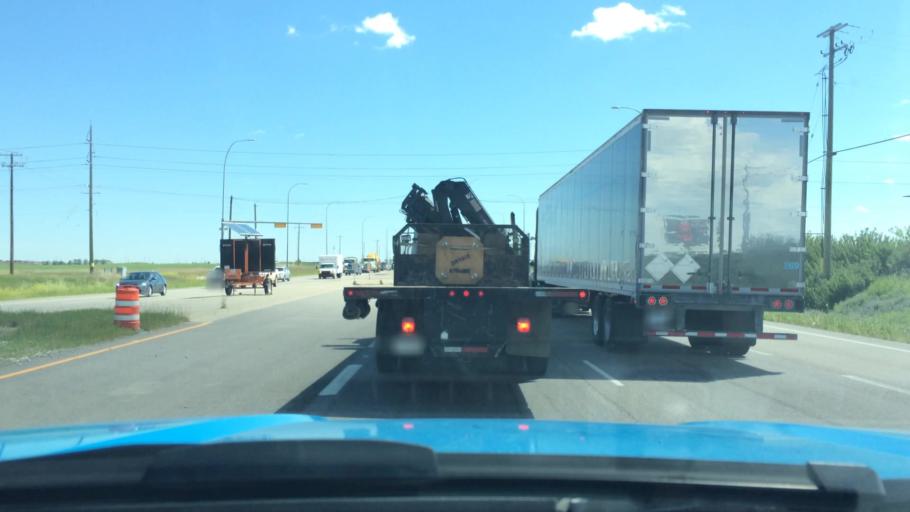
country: CA
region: Alberta
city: Chestermere
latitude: 50.9795
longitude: -113.9369
